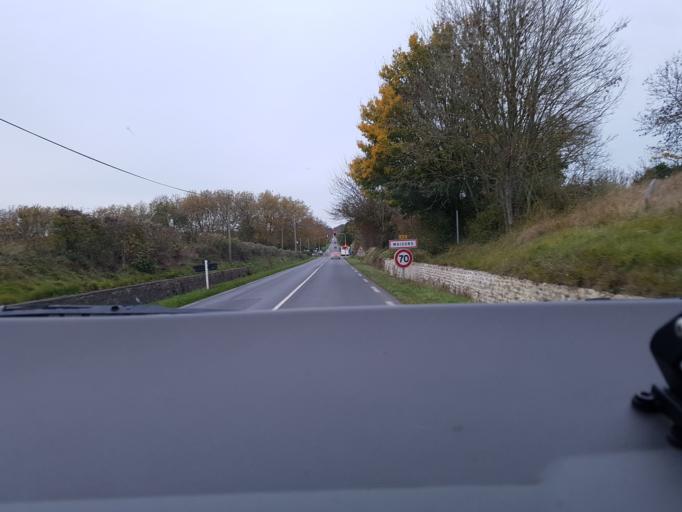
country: FR
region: Lower Normandy
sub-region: Departement du Calvados
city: Port-en-Bessin-Huppain
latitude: 49.3168
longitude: -0.7434
